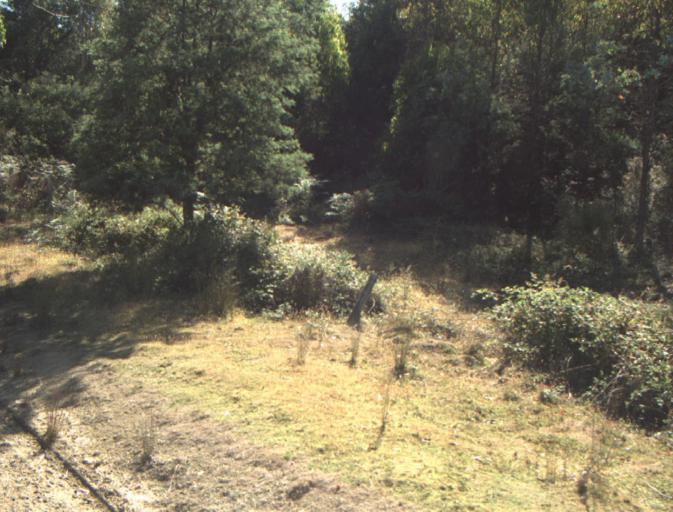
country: AU
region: Tasmania
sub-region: Dorset
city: Scottsdale
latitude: -41.2713
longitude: 147.3760
